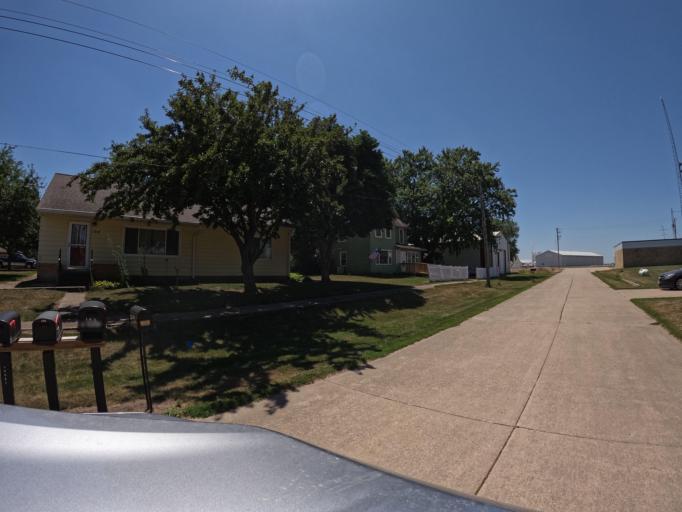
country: US
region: Iowa
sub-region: Poweshiek County
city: Montezuma
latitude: 41.4802
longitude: -92.3925
